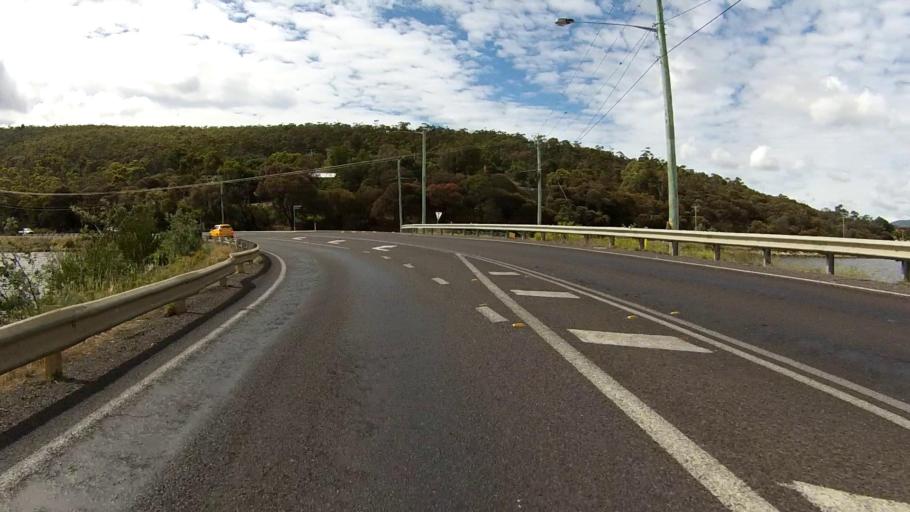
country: AU
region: Tasmania
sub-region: Glenorchy
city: Lutana
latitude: -42.8175
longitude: 147.3206
